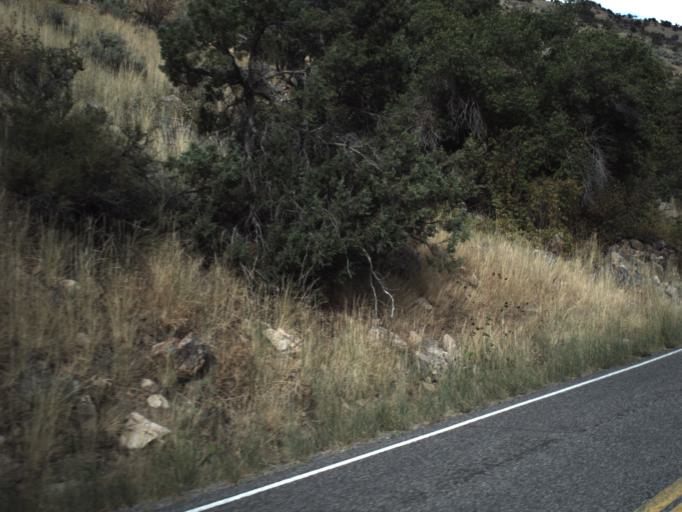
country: US
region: Utah
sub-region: Cache County
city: Millville
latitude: 41.6081
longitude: -111.6115
